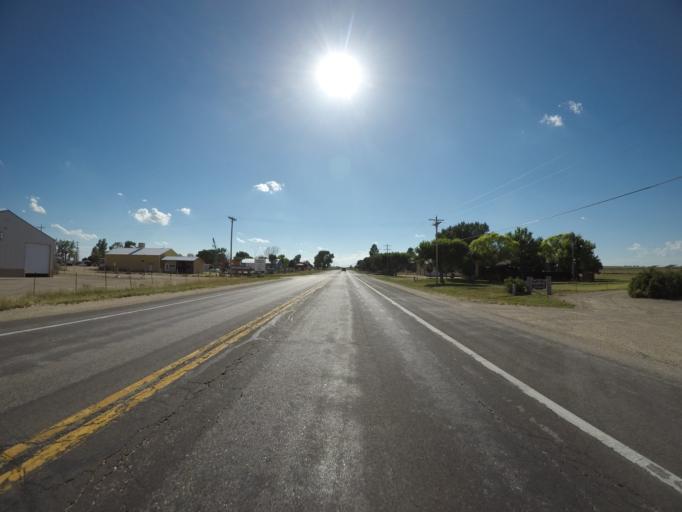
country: US
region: Colorado
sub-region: Logan County
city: Sterling
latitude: 40.6239
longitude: -103.3001
